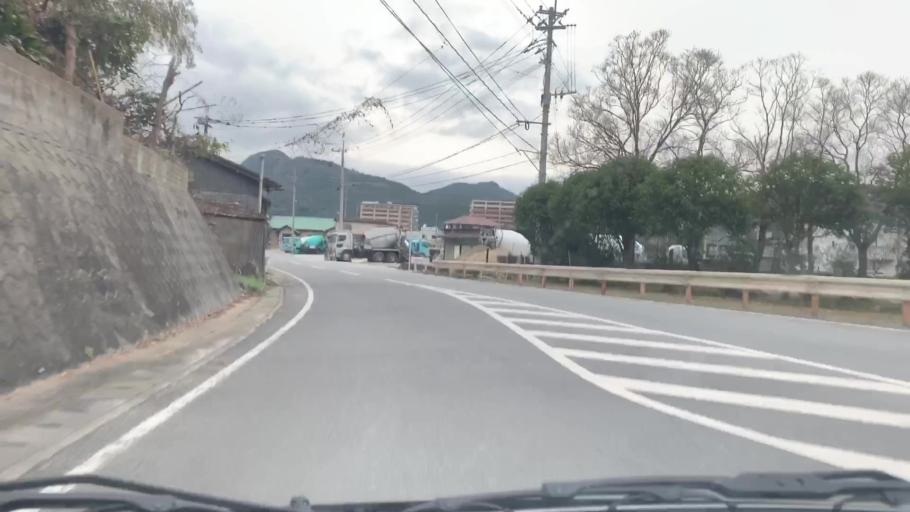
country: JP
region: Saga Prefecture
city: Takeocho-takeo
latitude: 33.1899
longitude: 130.0264
